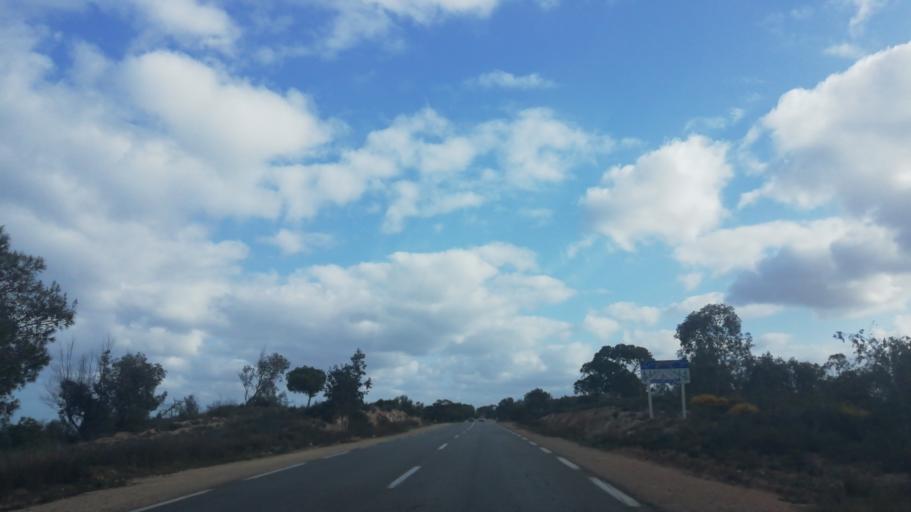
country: DZ
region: Relizane
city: Mazouna
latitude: 36.2345
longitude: 0.5225
